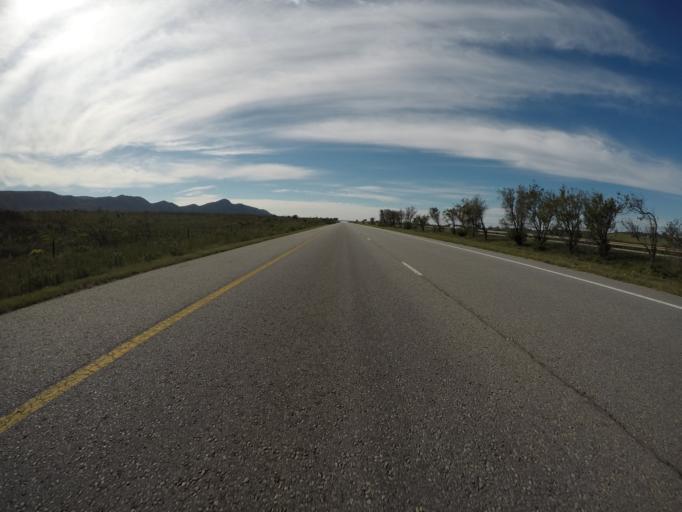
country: ZA
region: Eastern Cape
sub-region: Nelson Mandela Bay Metropolitan Municipality
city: Uitenhage
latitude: -33.9103
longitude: 25.2085
